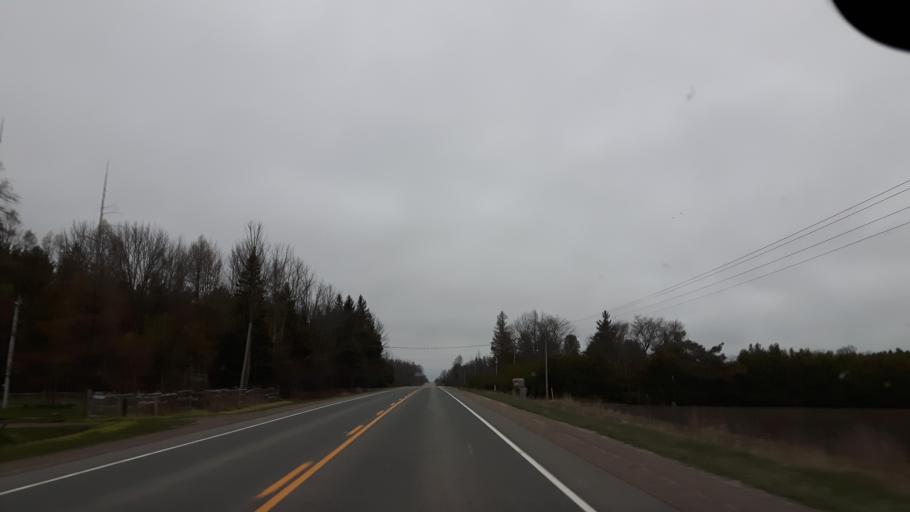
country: CA
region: Ontario
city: Goderich
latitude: 43.6708
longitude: -81.7057
